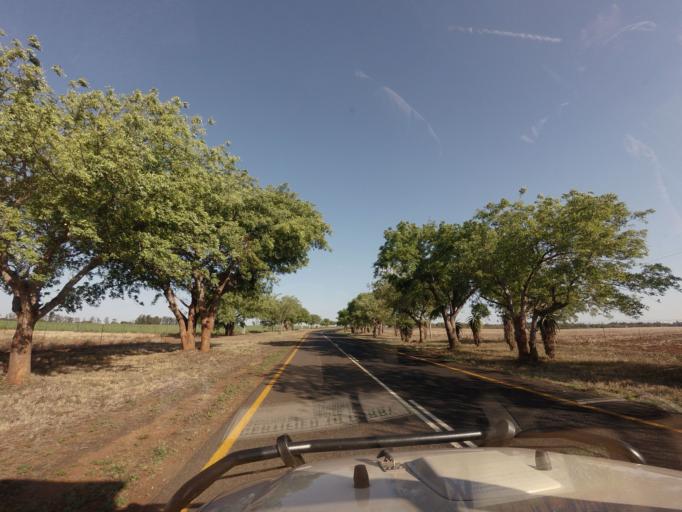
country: ZA
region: Mpumalanga
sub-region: Ehlanzeni District
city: Komatipoort
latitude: -25.3653
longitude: 31.8993
